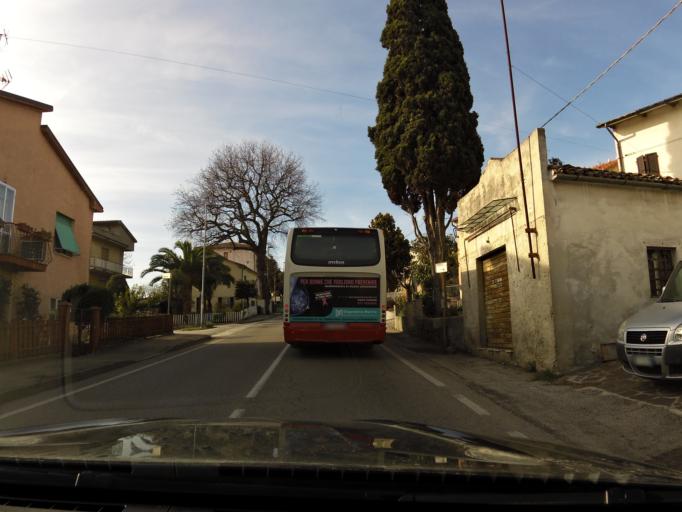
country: IT
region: The Marches
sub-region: Provincia di Ancona
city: Villa Musone
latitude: 43.4607
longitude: 13.5810
